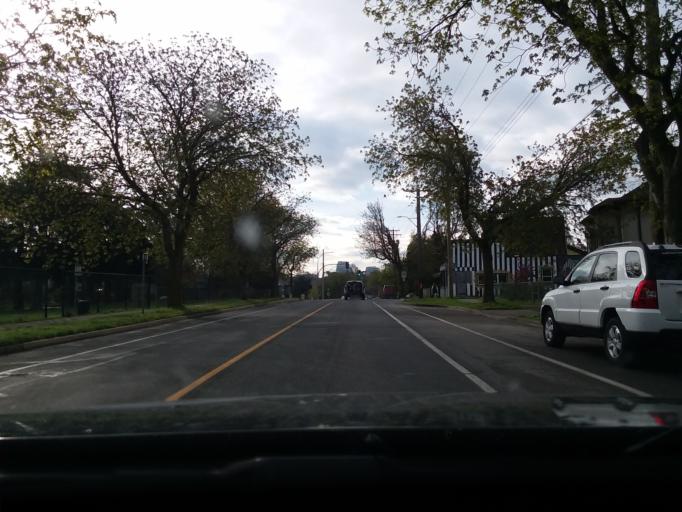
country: CA
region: British Columbia
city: Victoria
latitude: 48.4380
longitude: -123.3896
